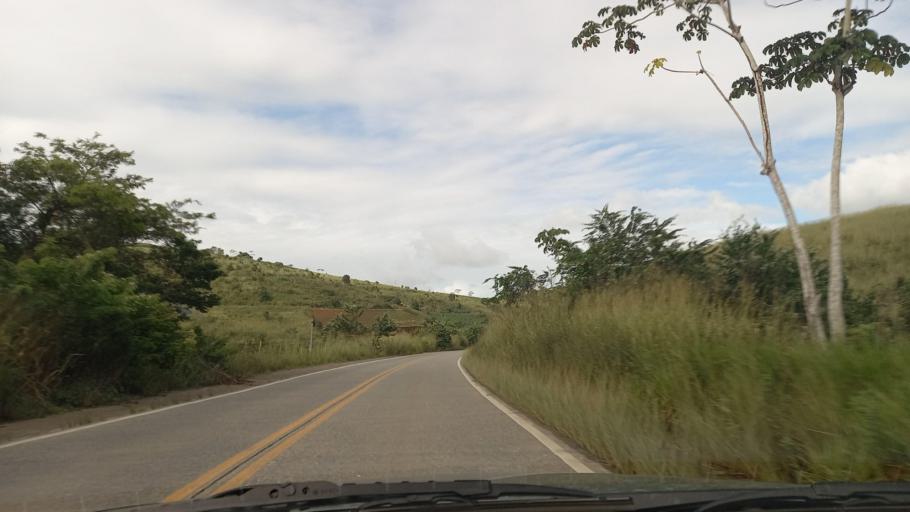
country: BR
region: Pernambuco
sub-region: Catende
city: Catende
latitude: -8.6895
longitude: -35.7073
